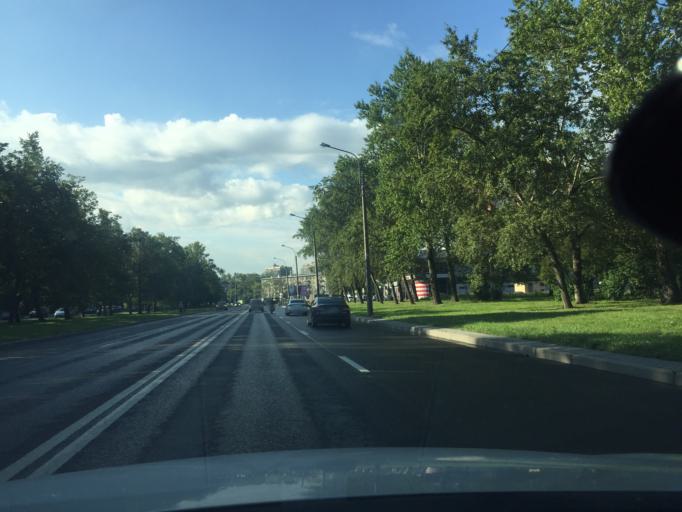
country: RU
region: St.-Petersburg
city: Kupchino
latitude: 59.8418
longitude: 30.3381
